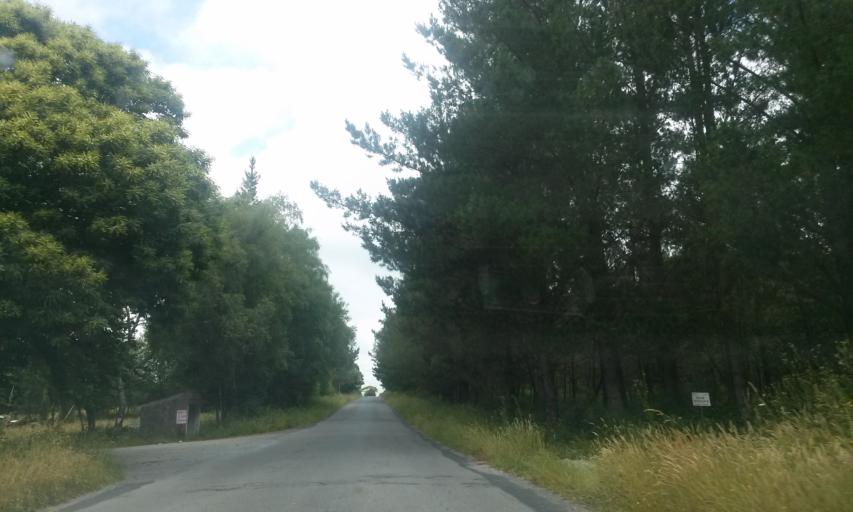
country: ES
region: Galicia
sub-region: Provincia de Lugo
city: Friol
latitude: 43.0798
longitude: -7.8165
